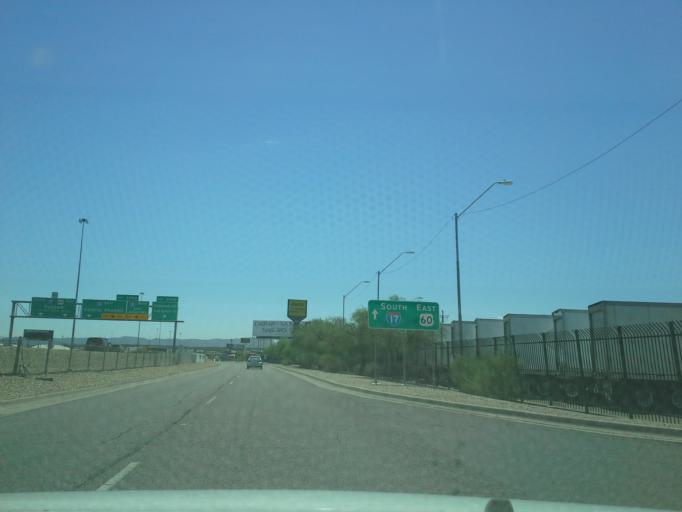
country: US
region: Arizona
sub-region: Maricopa County
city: Phoenix
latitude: 33.4718
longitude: -112.1128
